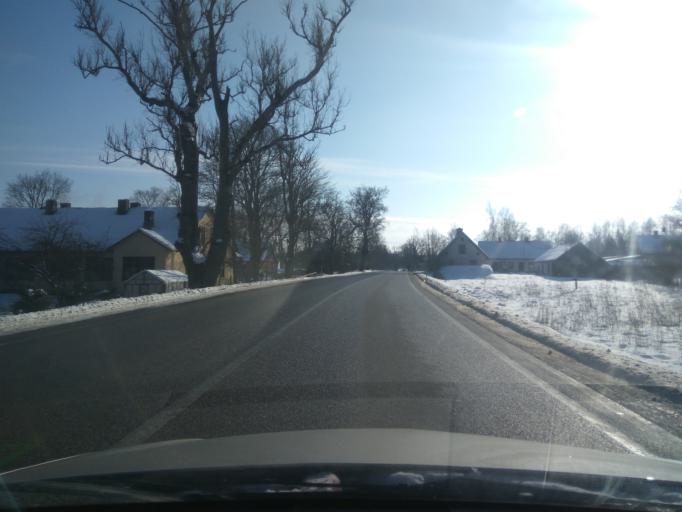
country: LV
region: Kuldigas Rajons
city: Kuldiga
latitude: 57.2822
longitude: 22.0235
